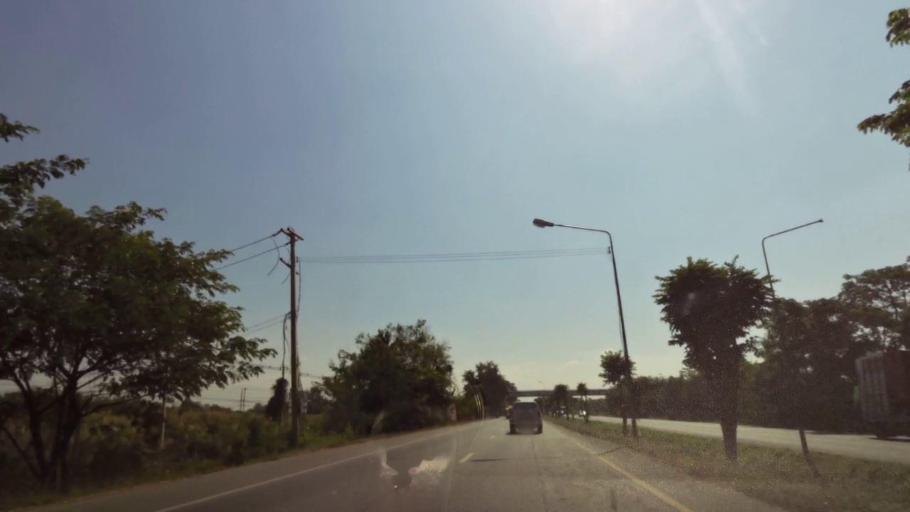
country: TH
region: Nakhon Sawan
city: Kao Liao
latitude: 15.7956
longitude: 100.1207
